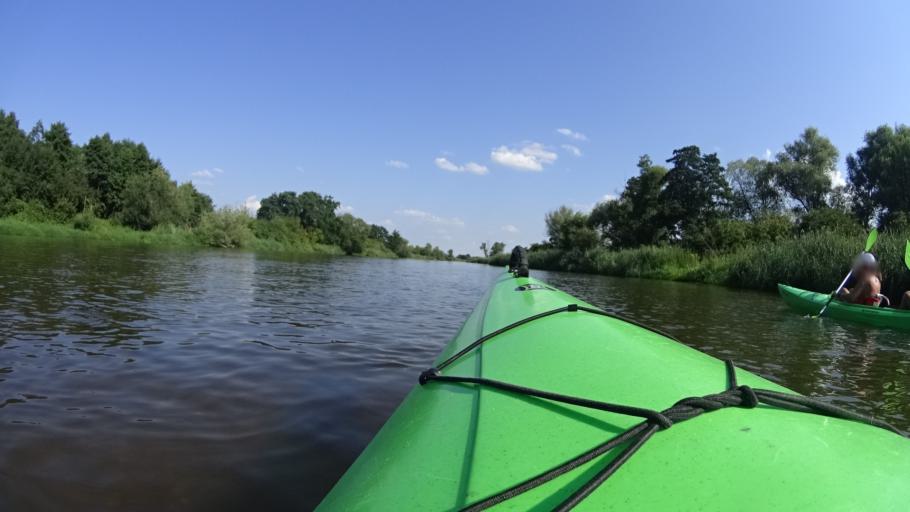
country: PL
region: Masovian Voivodeship
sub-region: Powiat bialobrzeski
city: Bialobrzegi
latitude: 51.6641
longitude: 20.9228
